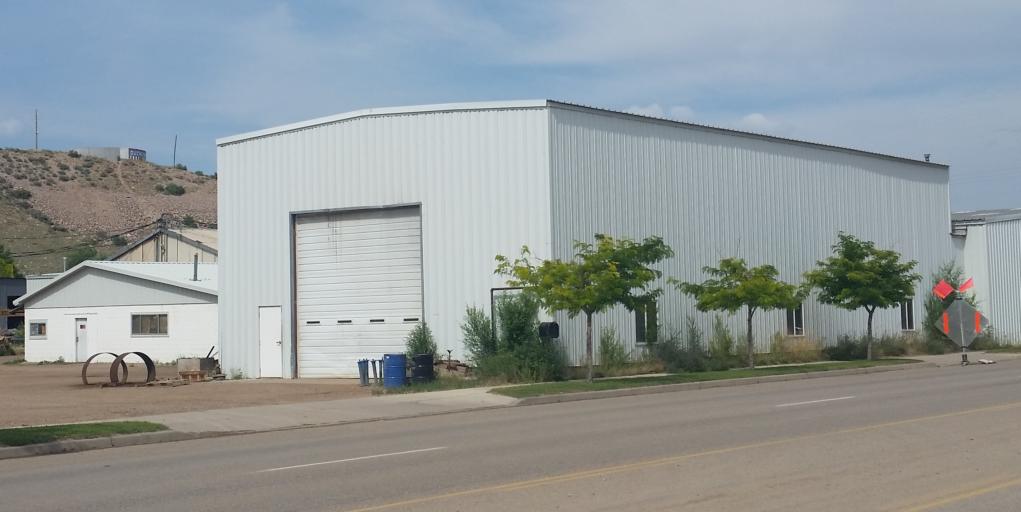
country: US
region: Utah
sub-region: Duchesne County
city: Duchesne
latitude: 40.1634
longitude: -110.4106
